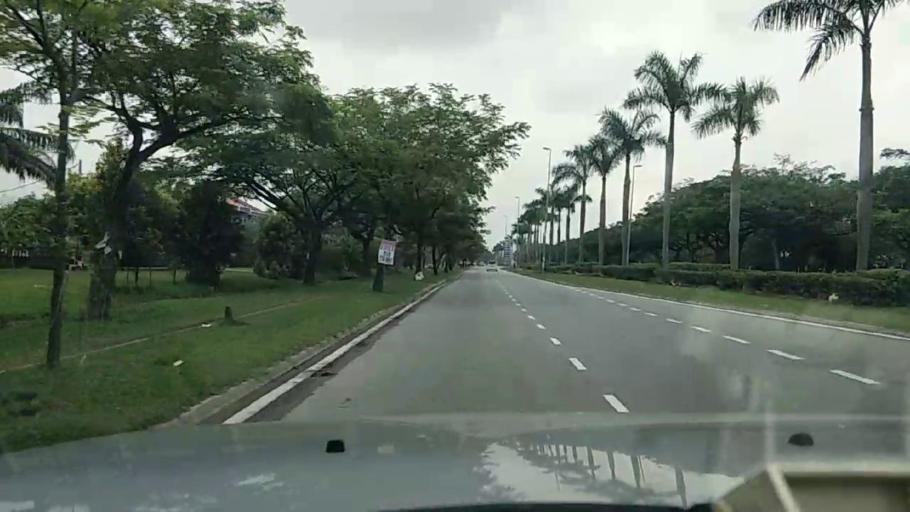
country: MY
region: Putrajaya
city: Putrajaya
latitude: 2.9428
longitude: 101.6176
